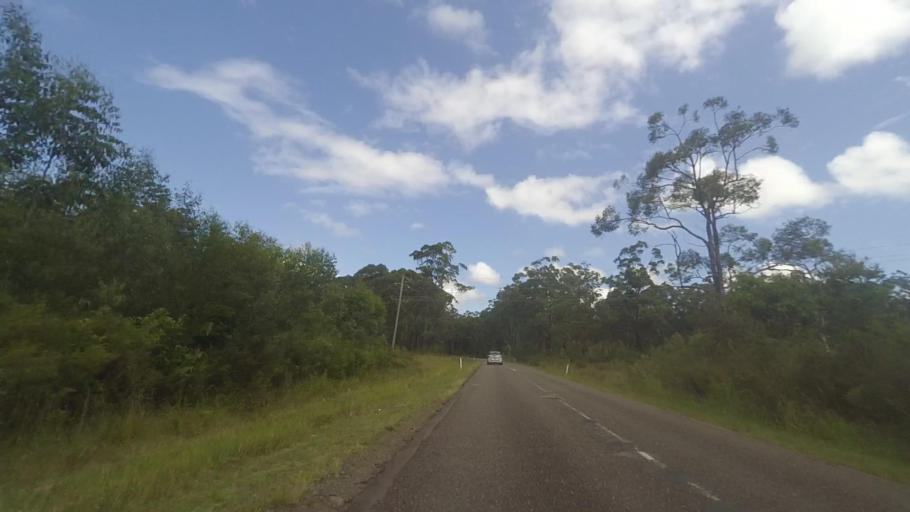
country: AU
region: New South Wales
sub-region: Great Lakes
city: Bulahdelah
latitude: -32.3963
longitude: 152.2533
